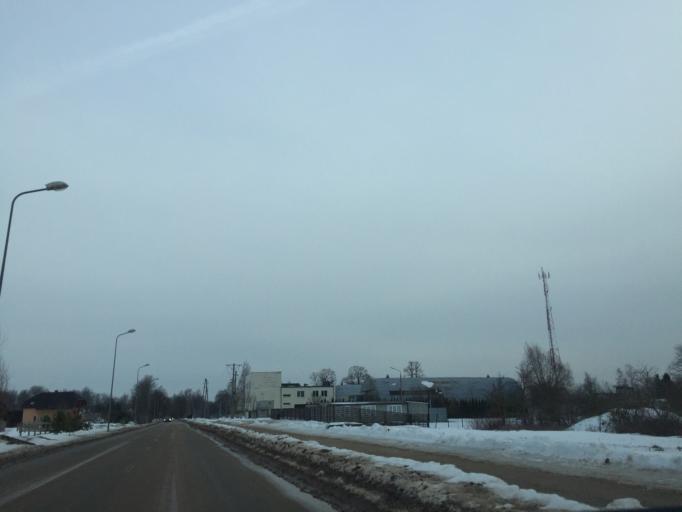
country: LV
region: Ikskile
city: Ikskile
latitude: 56.8332
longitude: 24.4819
